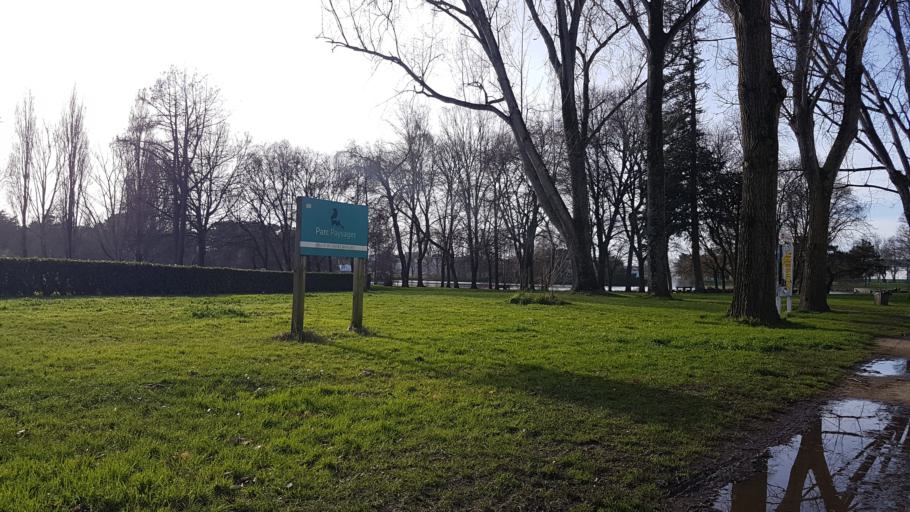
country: FR
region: Pays de la Loire
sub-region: Departement de la Loire-Atlantique
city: Saint-Nazaire
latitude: 47.2736
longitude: -2.2232
